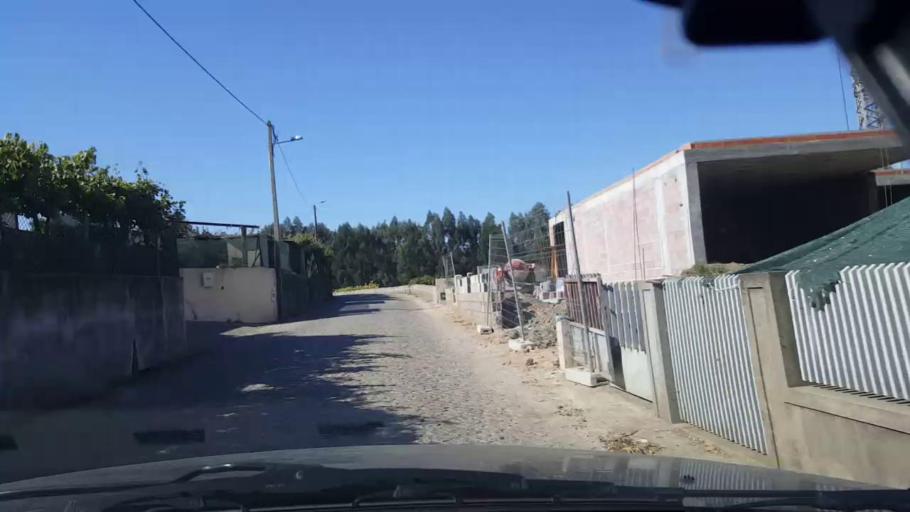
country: PT
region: Braga
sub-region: Vila Nova de Famalicao
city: Ribeirao
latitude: 41.3789
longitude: -8.6378
